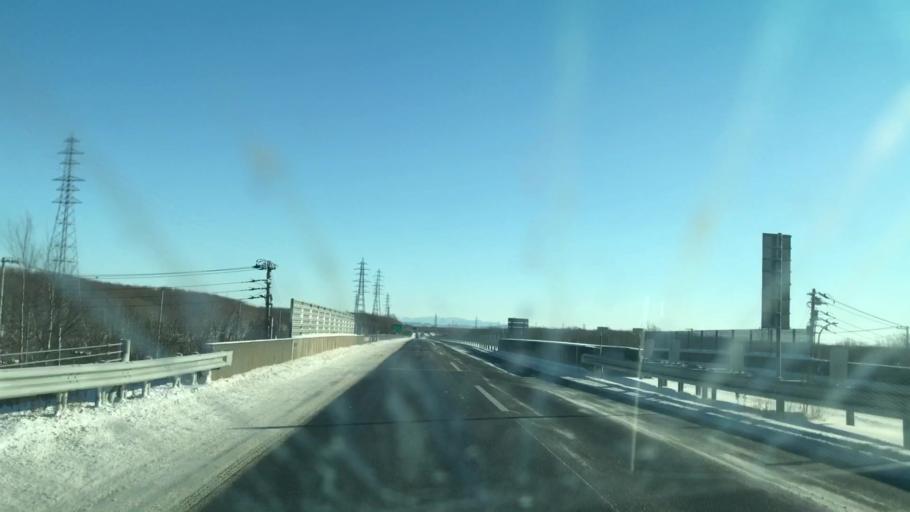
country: JP
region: Hokkaido
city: Tomakomai
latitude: 42.6734
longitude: 141.7659
